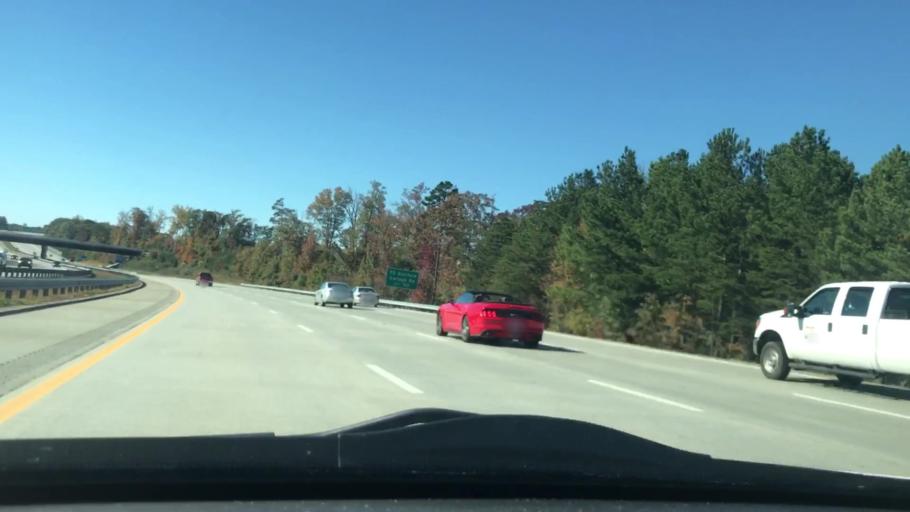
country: US
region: North Carolina
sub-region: Guilford County
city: Jamestown
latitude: 36.0446
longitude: -79.8981
